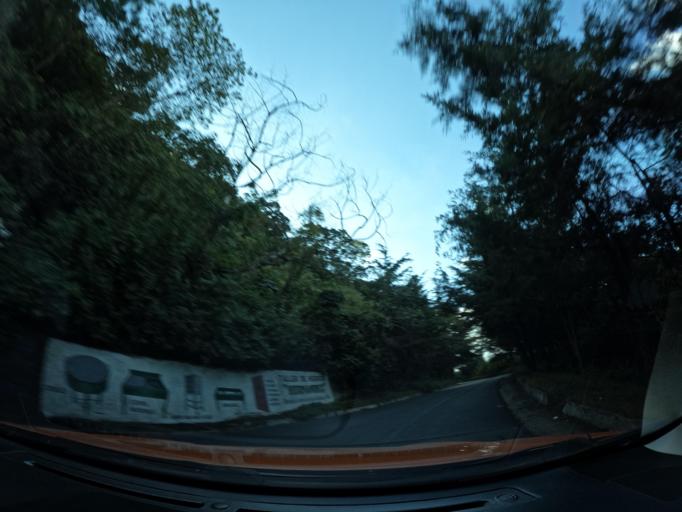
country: GT
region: Sacatepequez
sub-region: Municipio de Santa Maria de Jesus
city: Santa Maria de Jesus
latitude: 14.5116
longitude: -90.7198
